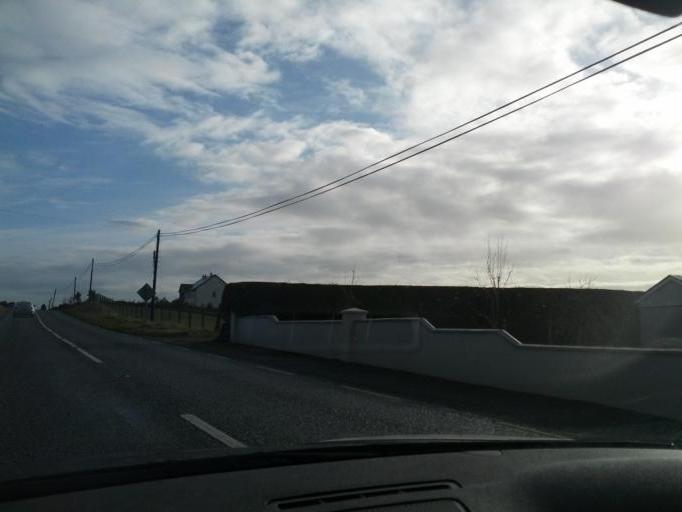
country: IE
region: Connaught
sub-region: County Galway
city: Athenry
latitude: 53.3598
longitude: -8.7330
